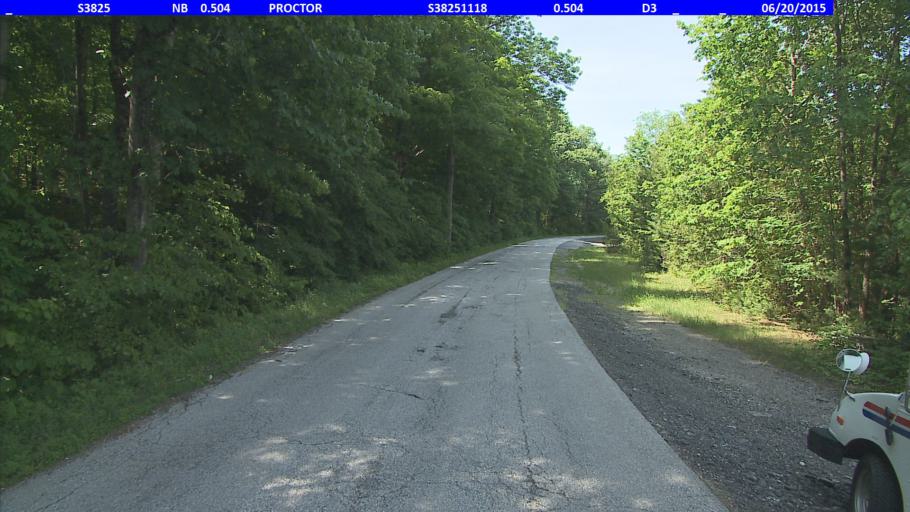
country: US
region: Vermont
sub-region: Rutland County
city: West Rutland
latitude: 43.6658
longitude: -73.0474
